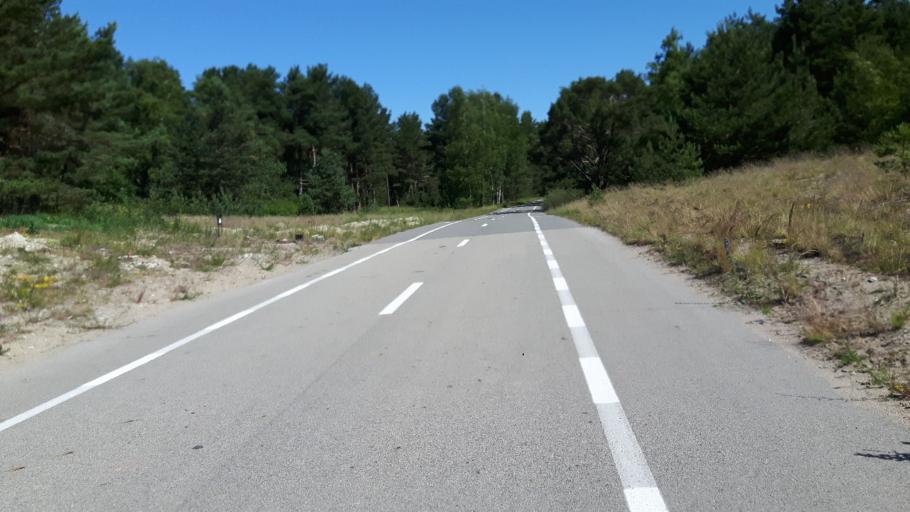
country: LT
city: Nida
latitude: 55.3212
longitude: 21.0238
